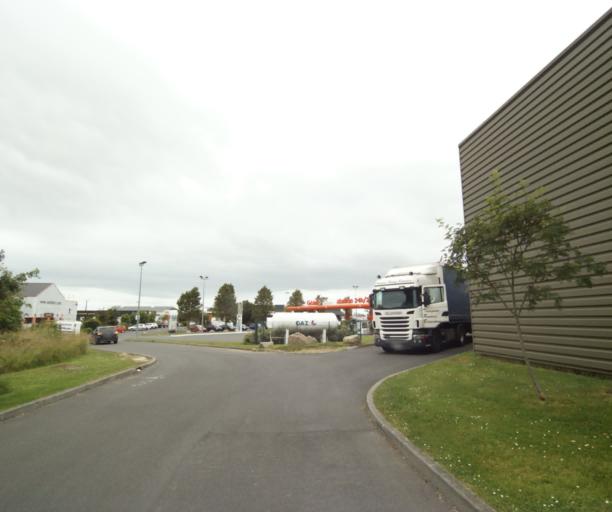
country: FR
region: Lower Normandy
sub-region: Departement du Calvados
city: Dives-sur-Mer
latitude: 49.2750
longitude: -0.1034
